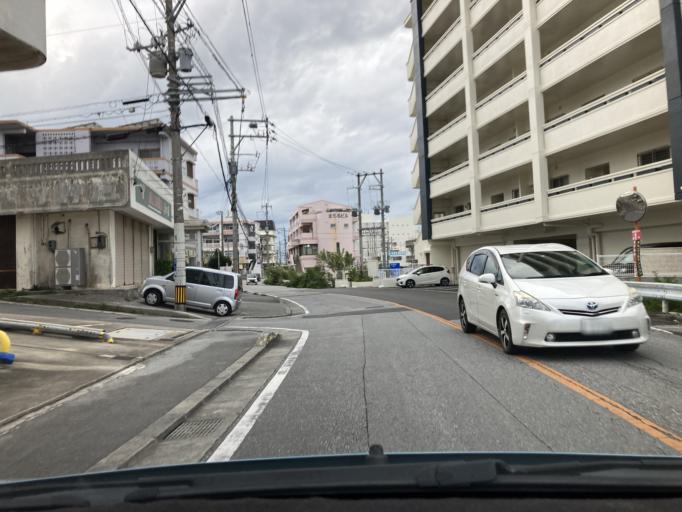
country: JP
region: Okinawa
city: Tomigusuku
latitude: 26.1768
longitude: 127.6842
